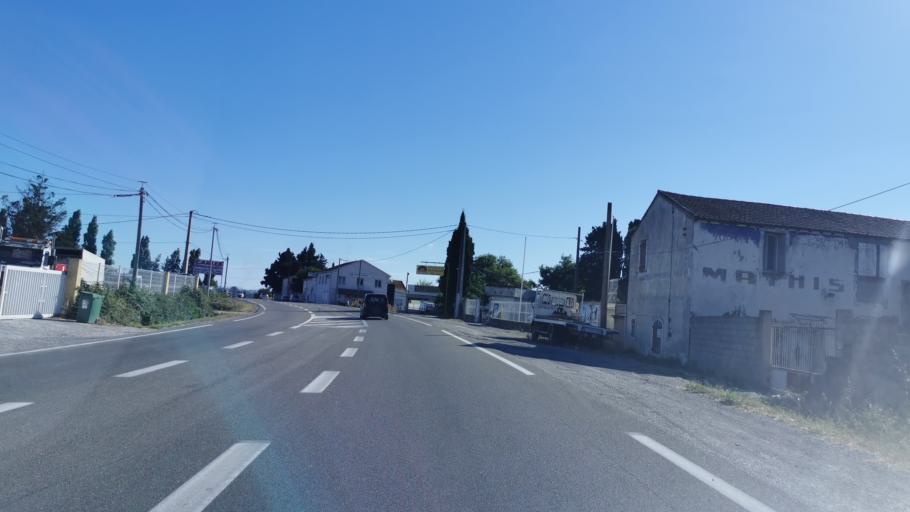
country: FR
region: Languedoc-Roussillon
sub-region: Departement de l'Herault
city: Beziers
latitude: 43.3171
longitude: 3.1840
